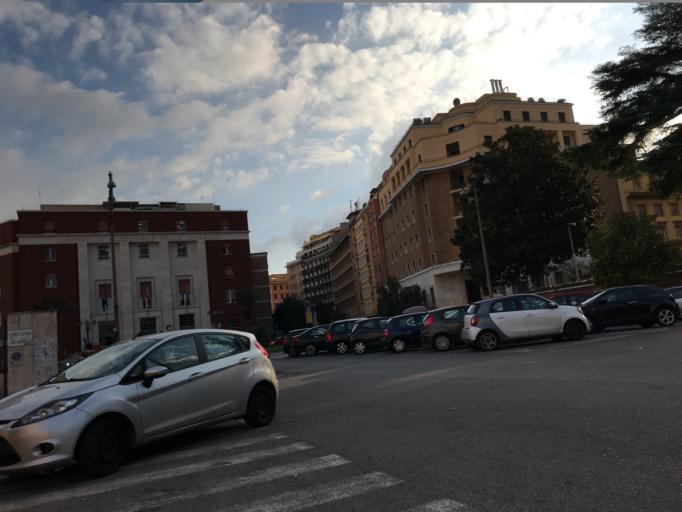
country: IT
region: Latium
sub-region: Citta metropolitana di Roma Capitale
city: Rome
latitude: 41.9017
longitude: 12.5123
